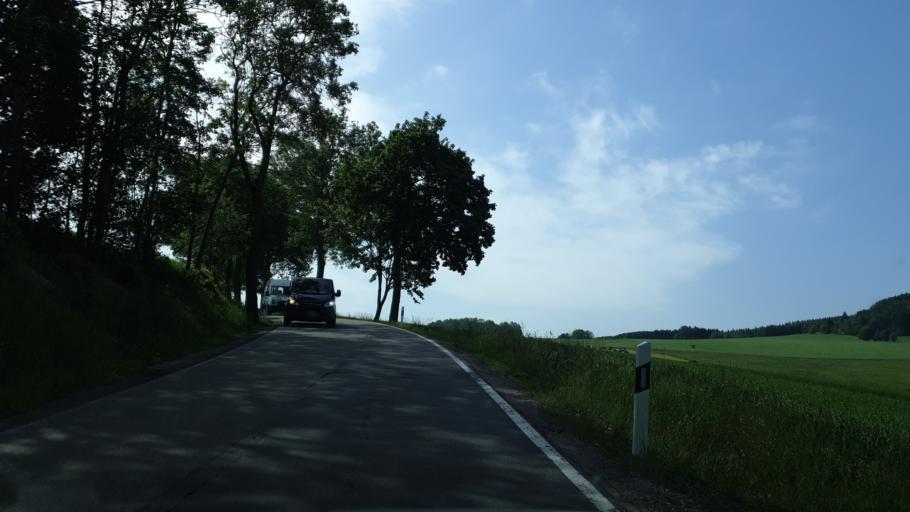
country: DE
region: Saxony
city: Zschorlau
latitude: 50.5593
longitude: 12.6456
